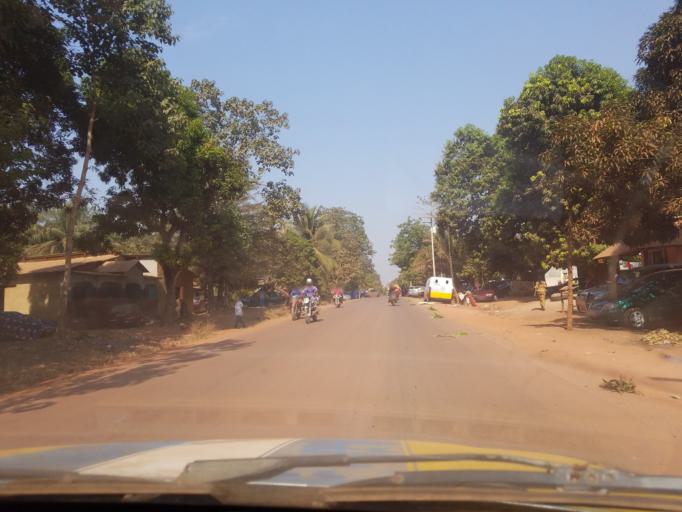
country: GN
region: Boke
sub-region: Boke Prefecture
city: Sangueya
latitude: 10.8045
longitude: -14.3896
